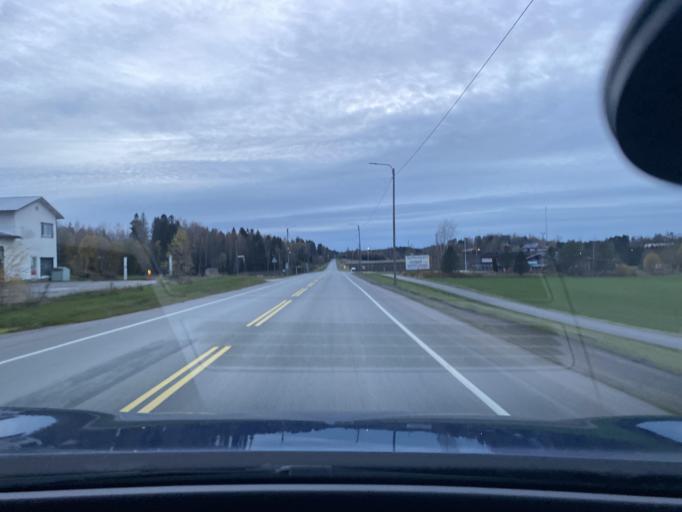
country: FI
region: Uusimaa
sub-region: Helsinki
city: Saukkola
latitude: 60.3860
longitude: 23.9070
